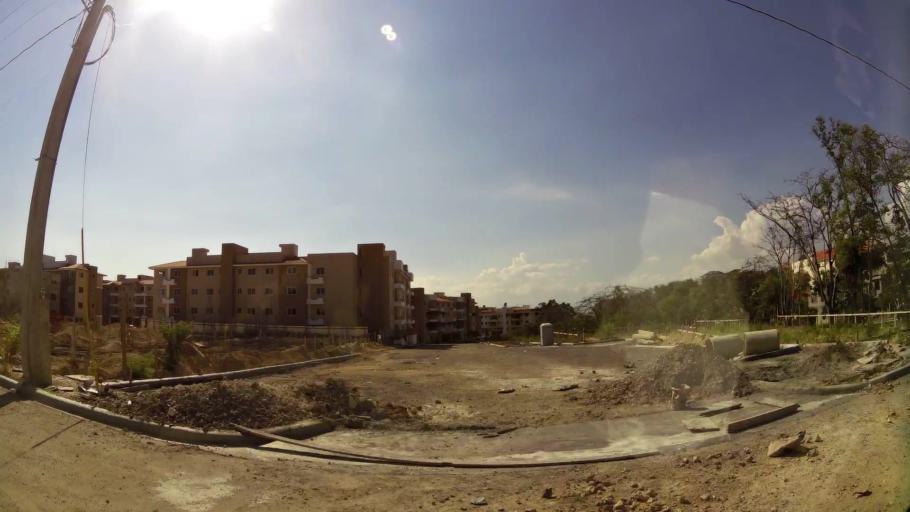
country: DO
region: Nacional
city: Bella Vista
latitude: 18.4589
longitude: -69.9810
